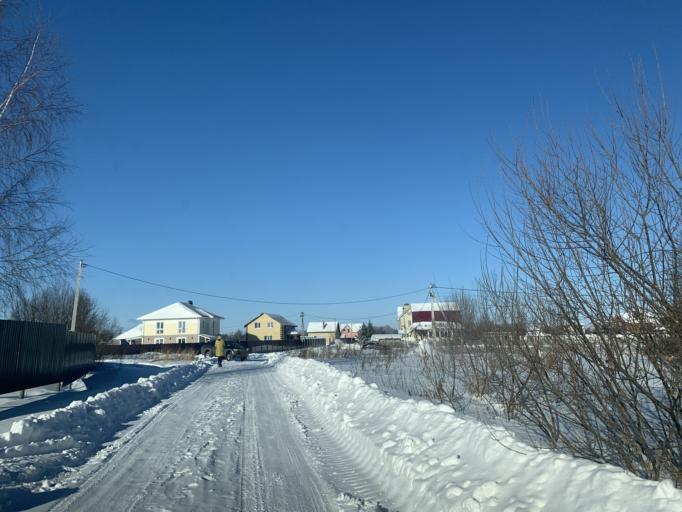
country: RU
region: Jaroslavl
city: Tunoshna
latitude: 57.6624
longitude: 40.0667
